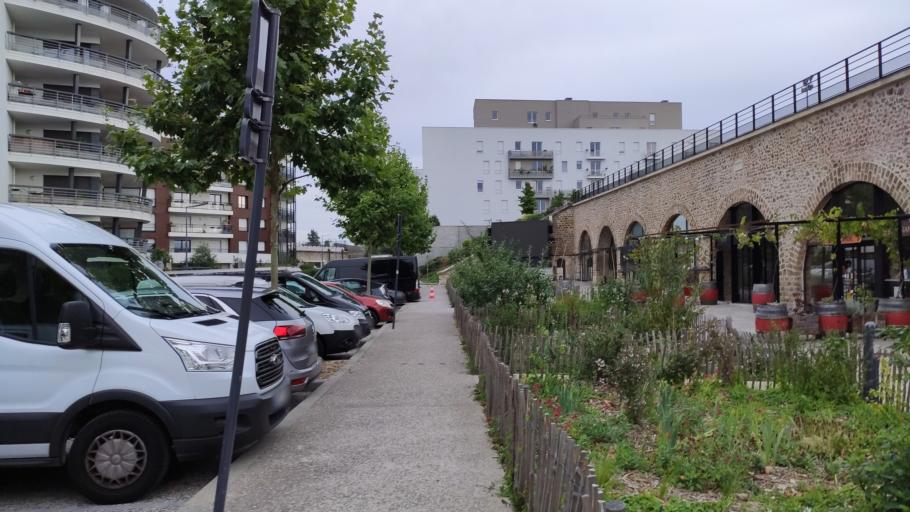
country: FR
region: Ile-de-France
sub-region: Departement des Hauts-de-Seine
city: Issy-les-Moulineaux
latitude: 48.8176
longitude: 2.2666
